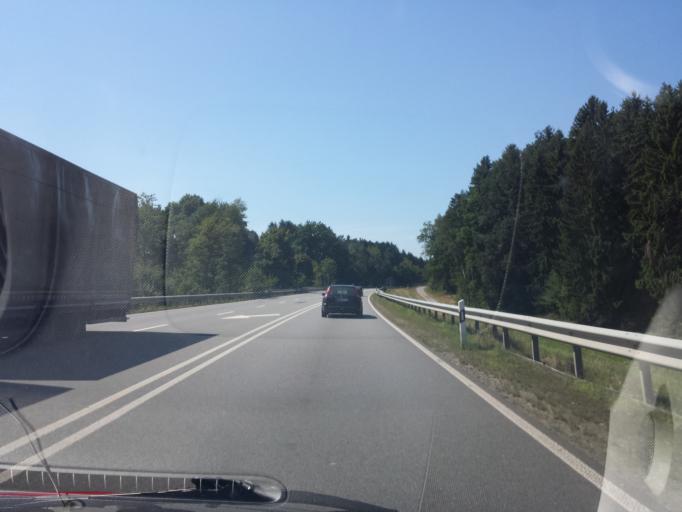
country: DE
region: Bavaria
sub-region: Upper Palatinate
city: Weiding
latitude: 49.2716
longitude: 12.7751
